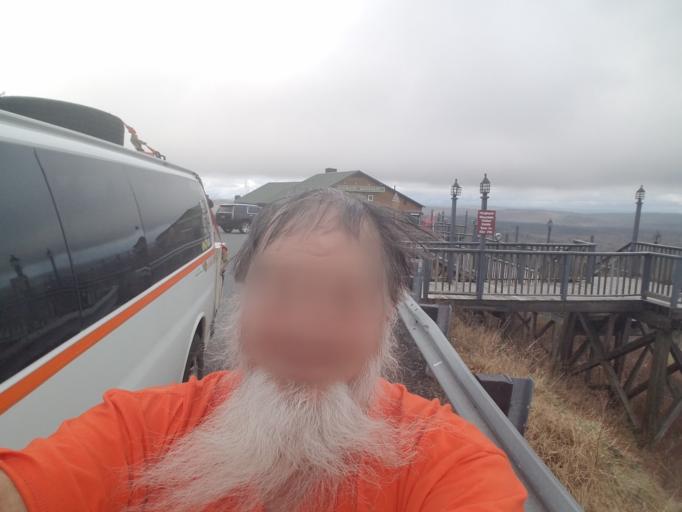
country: US
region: Vermont
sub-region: Windham County
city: Dover
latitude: 42.8525
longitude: -72.7936
